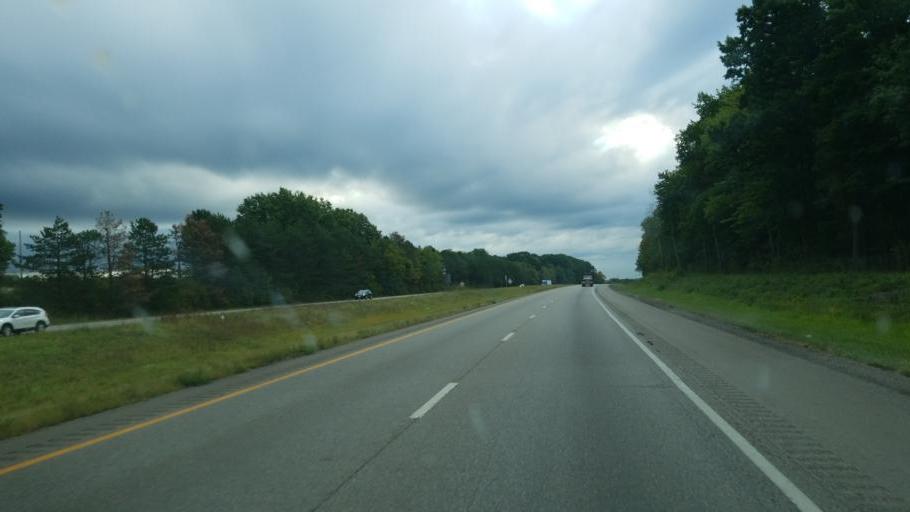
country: US
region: Ohio
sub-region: Trumbull County
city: Churchill
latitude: 41.1595
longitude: -80.6452
